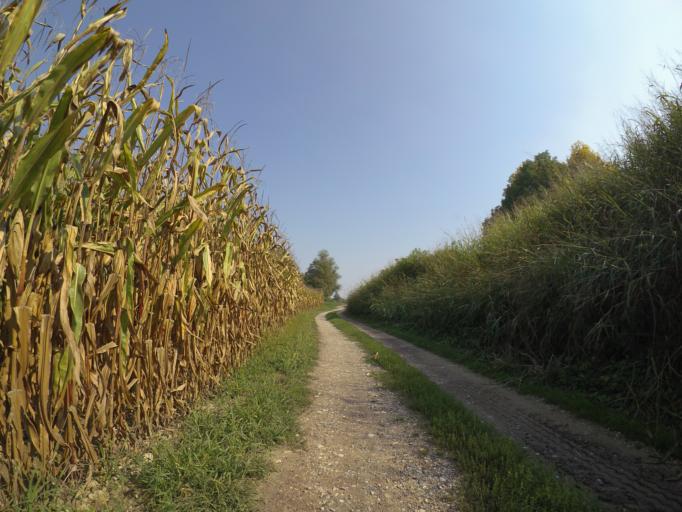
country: IT
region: Friuli Venezia Giulia
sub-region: Provincia di Udine
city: Varmo
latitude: 45.8826
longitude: 12.9739
